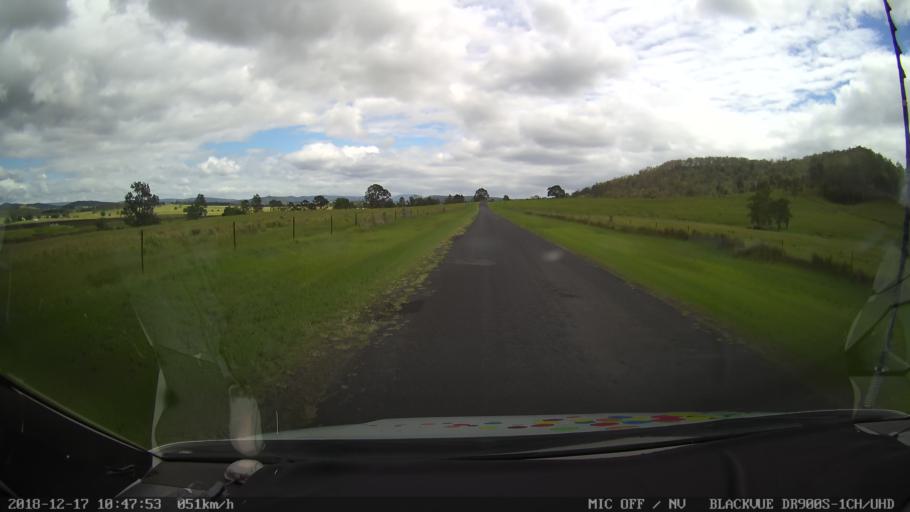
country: AU
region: New South Wales
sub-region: Clarence Valley
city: Gordon
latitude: -28.8776
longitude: 152.5705
